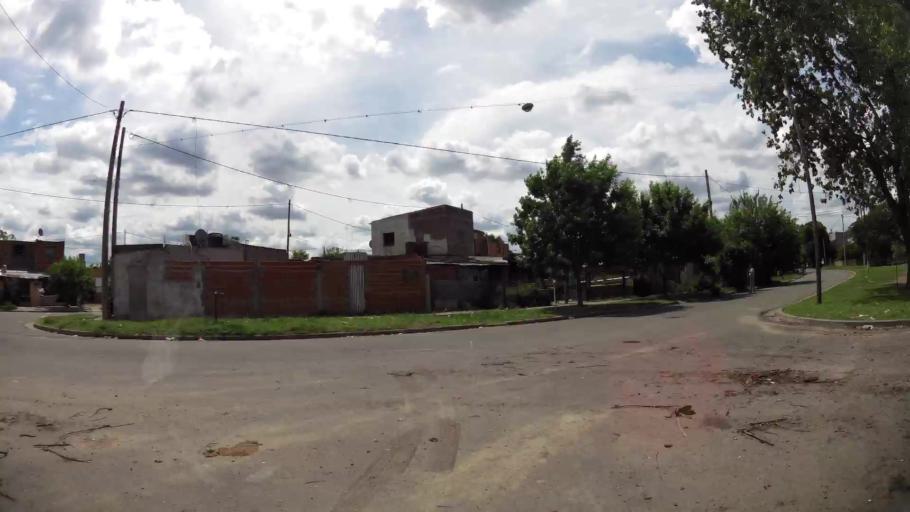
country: AR
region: Santa Fe
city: Gobernador Galvez
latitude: -33.0147
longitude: -60.6384
